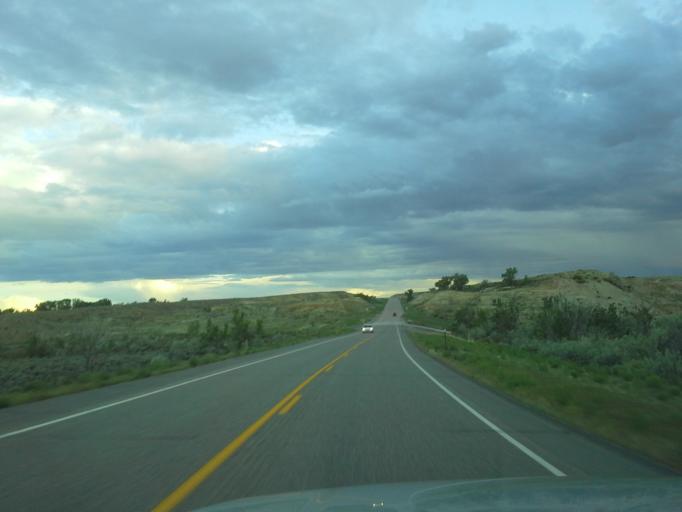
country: US
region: Wyoming
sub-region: Big Horn County
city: Basin
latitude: 44.3097
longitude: -108.0423
